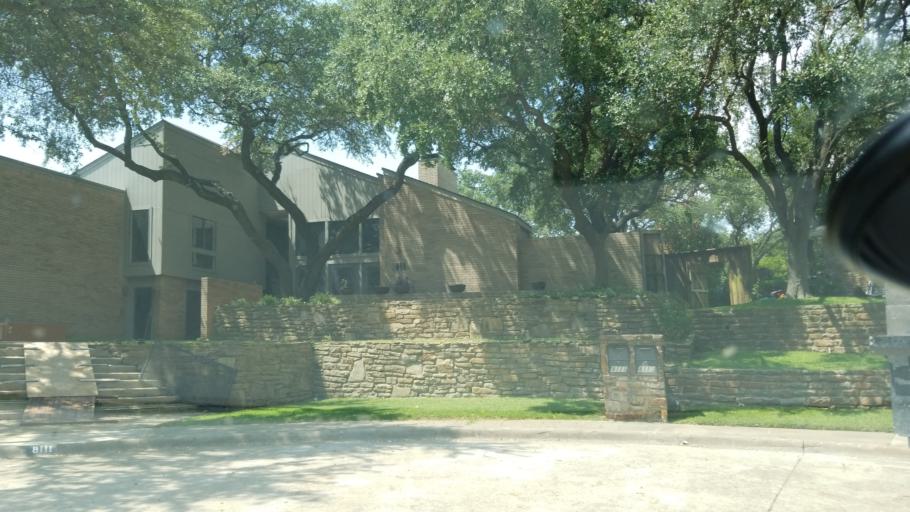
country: US
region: Texas
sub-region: Dallas County
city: Richardson
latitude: 32.8929
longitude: -96.7355
